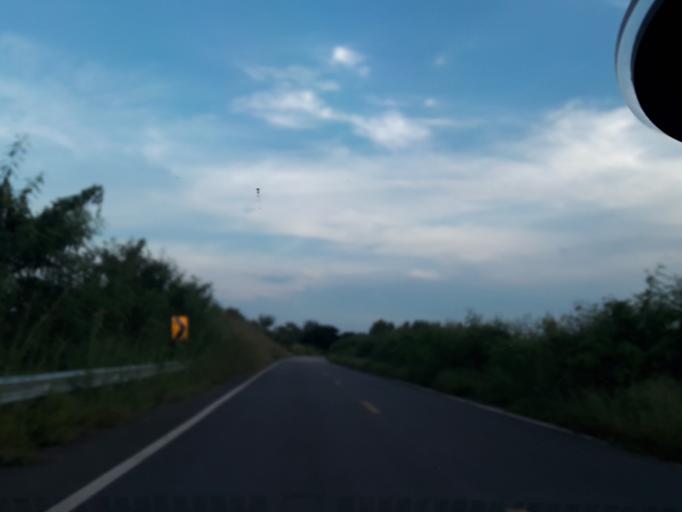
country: TH
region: Sara Buri
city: Nong Khae
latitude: 14.3014
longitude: 100.8898
